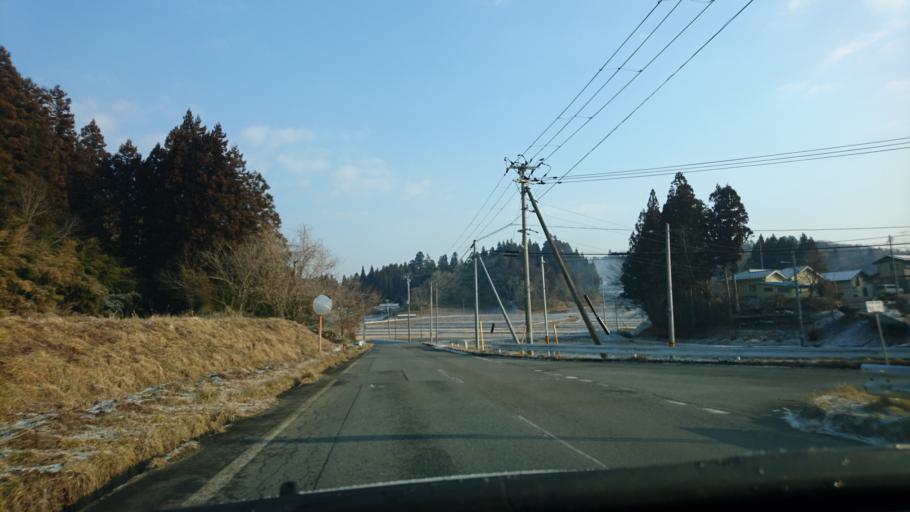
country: JP
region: Iwate
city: Ichinoseki
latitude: 38.9258
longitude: 141.3861
